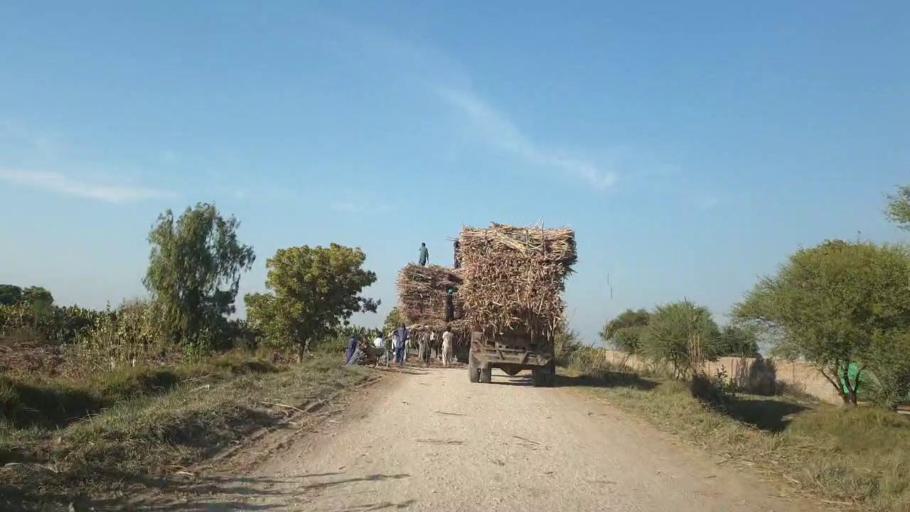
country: PK
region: Sindh
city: Tando Adam
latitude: 25.7185
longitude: 68.7033
